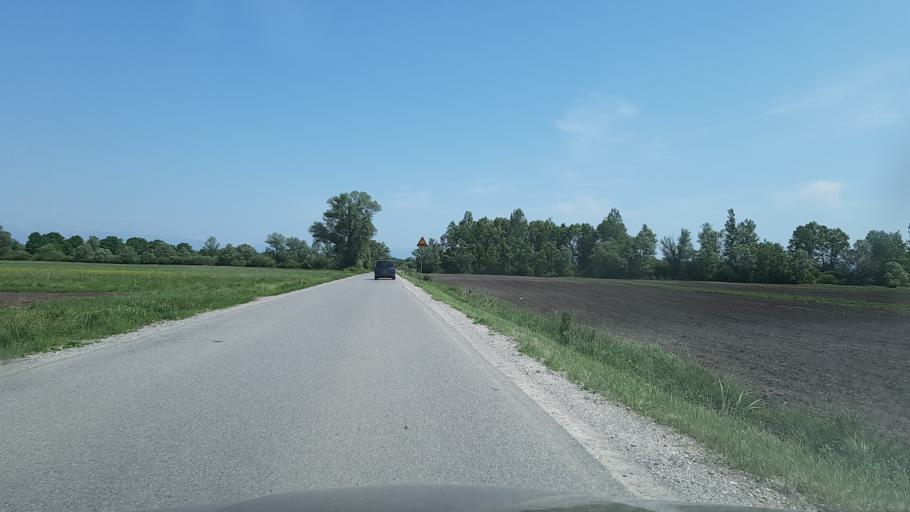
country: SI
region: Brezovica
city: Vnanje Gorice
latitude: 45.9837
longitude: 14.4357
